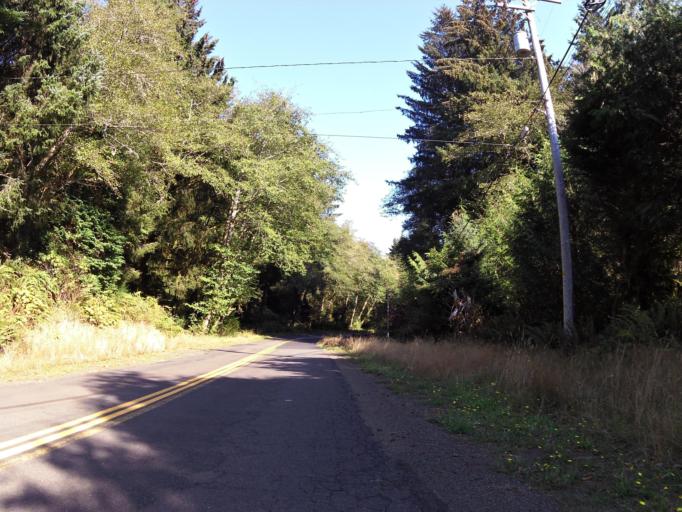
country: US
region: Oregon
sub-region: Lincoln County
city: Rose Lodge
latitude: 45.0801
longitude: -123.9431
